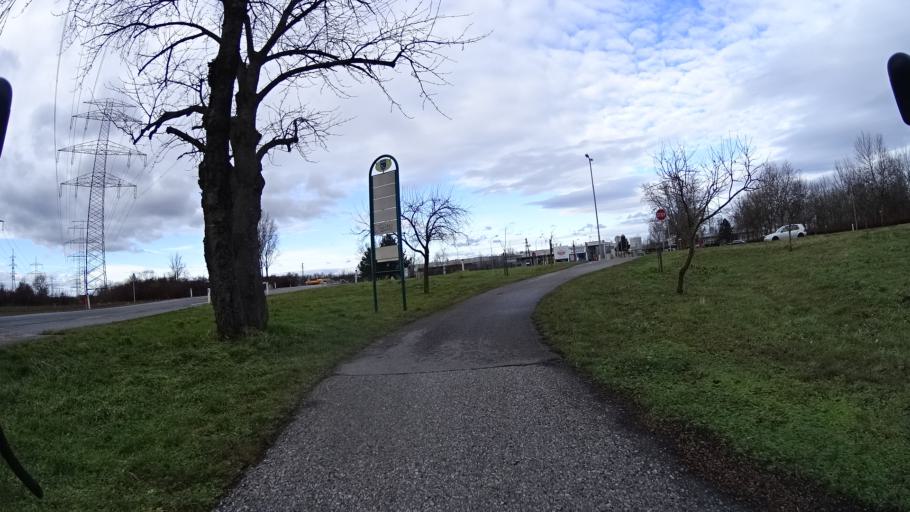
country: AT
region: Lower Austria
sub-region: Politischer Bezirk Tulln
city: Michelhausen
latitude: 48.3316
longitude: 15.9459
